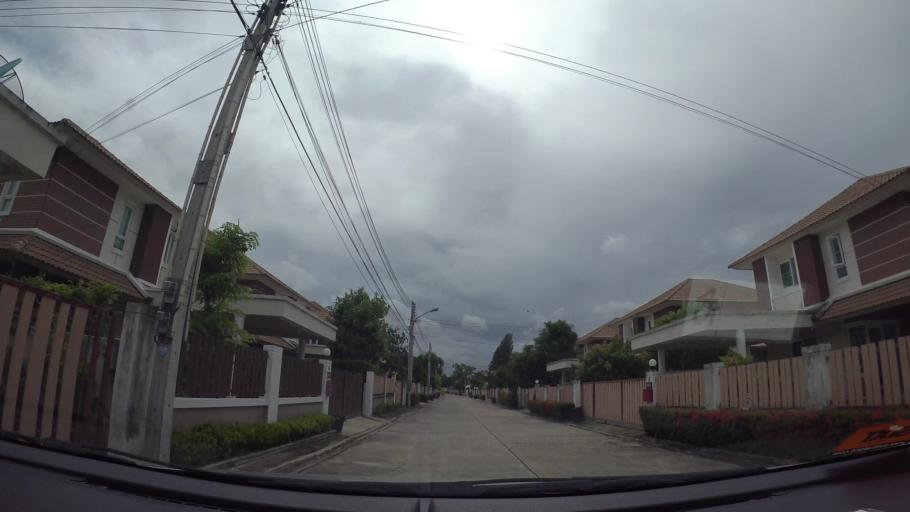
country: TH
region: Chon Buri
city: Si Racha
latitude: 13.1442
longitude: 100.9842
